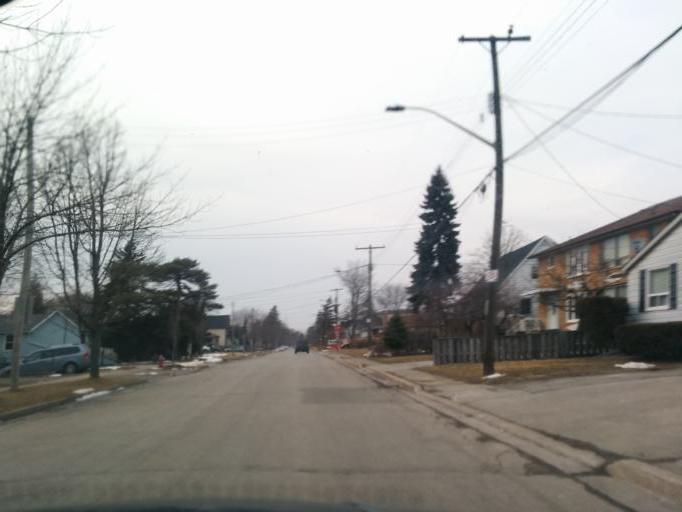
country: CA
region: Ontario
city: Etobicoke
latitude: 43.5803
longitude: -79.5686
